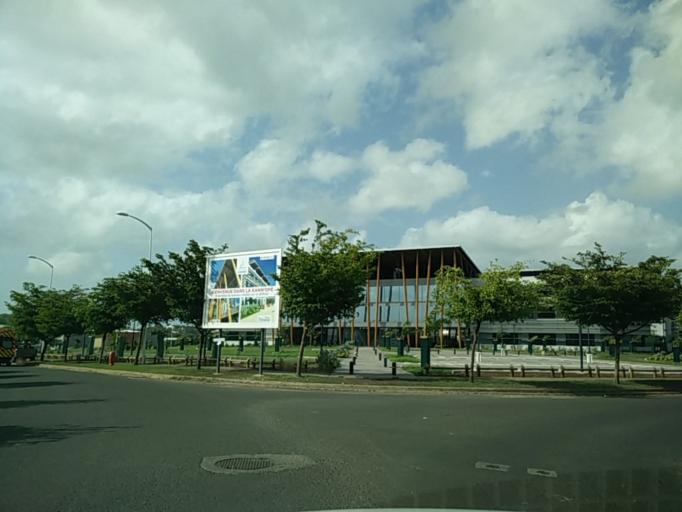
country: GP
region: Guadeloupe
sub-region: Guadeloupe
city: Les Abymes
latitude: 16.2781
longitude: -61.5106
